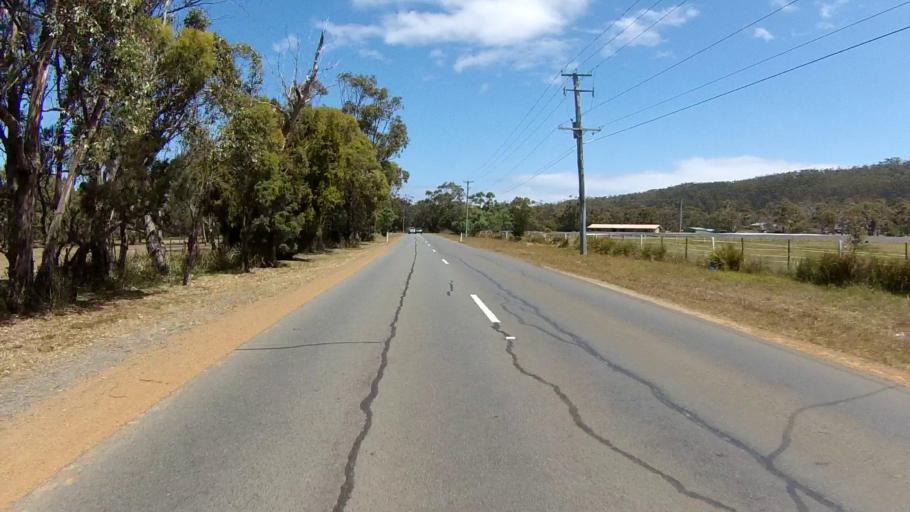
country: AU
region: Tasmania
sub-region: Clarence
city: Sandford
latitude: -42.9444
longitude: 147.4840
